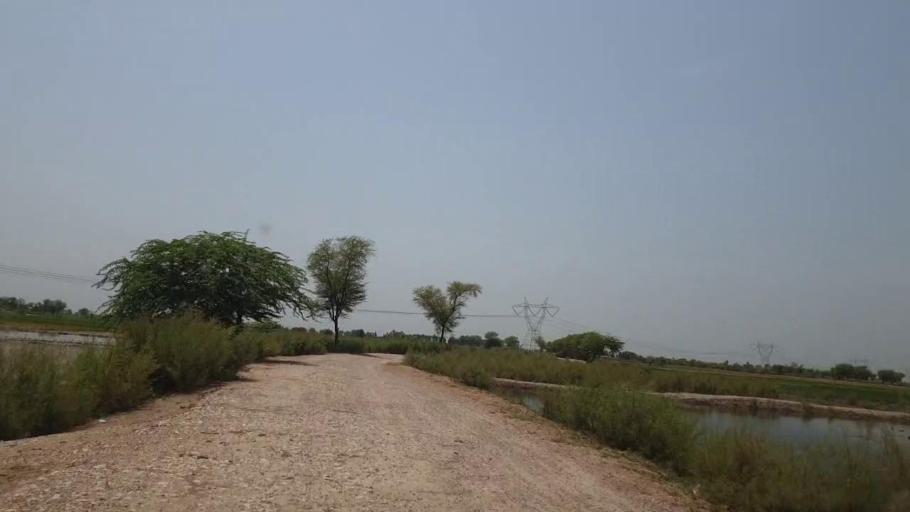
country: PK
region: Sindh
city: Shikarpur
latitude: 27.8914
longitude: 68.6309
